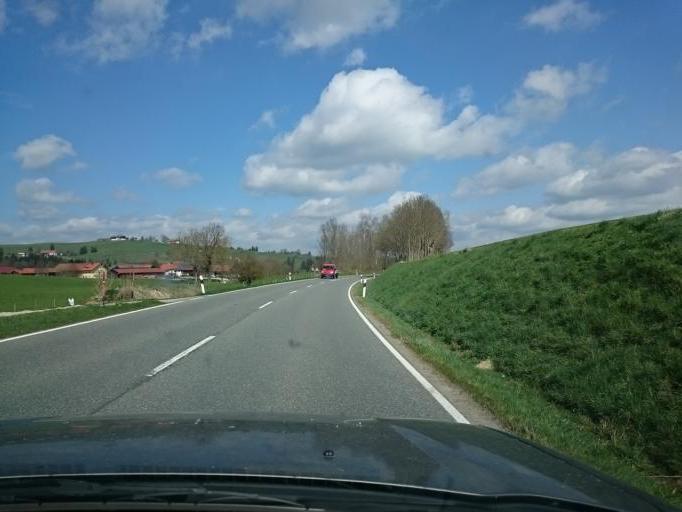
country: DE
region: Bavaria
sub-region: Upper Bavaria
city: Wildsteig
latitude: 47.7016
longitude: 10.9799
